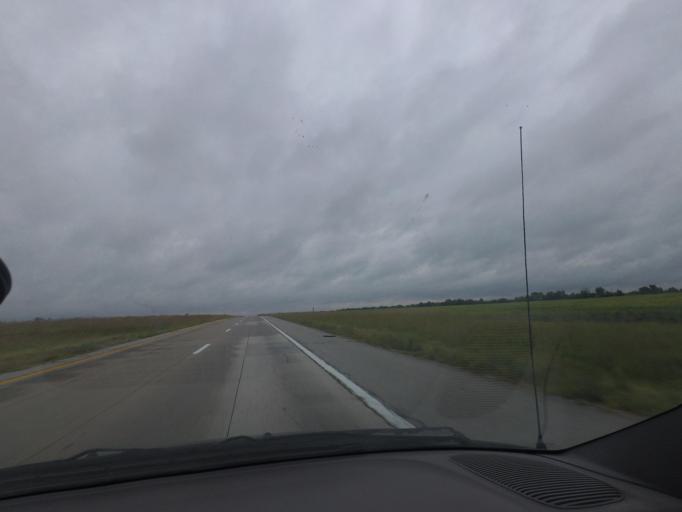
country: US
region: Missouri
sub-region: Marion County
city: Monroe City
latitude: 39.6582
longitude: -91.7909
